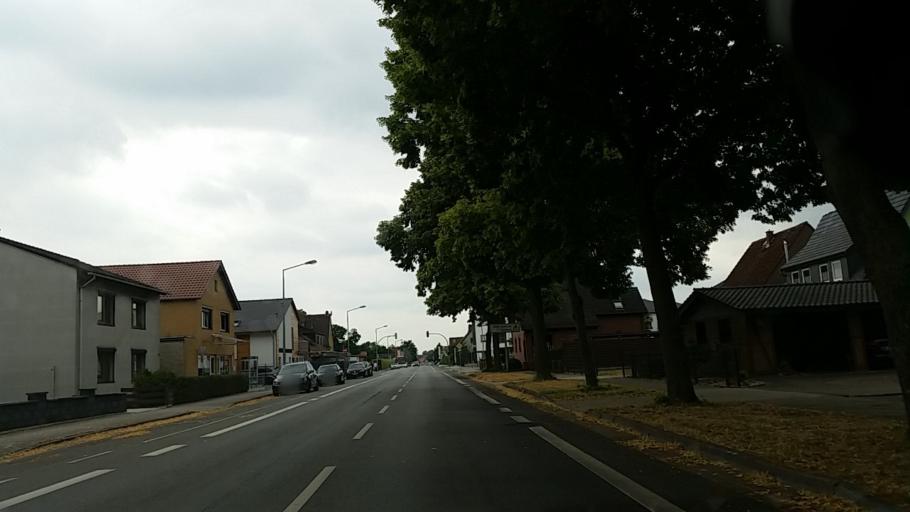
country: DE
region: Lower Saxony
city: Ruhen
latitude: 52.4488
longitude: 10.8475
